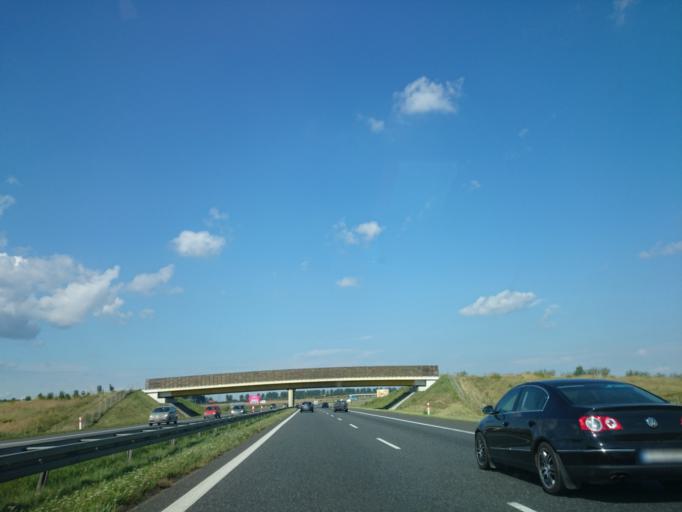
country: PL
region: Silesian Voivodeship
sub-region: Powiat gliwicki
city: Zernica
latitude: 50.2652
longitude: 18.6017
